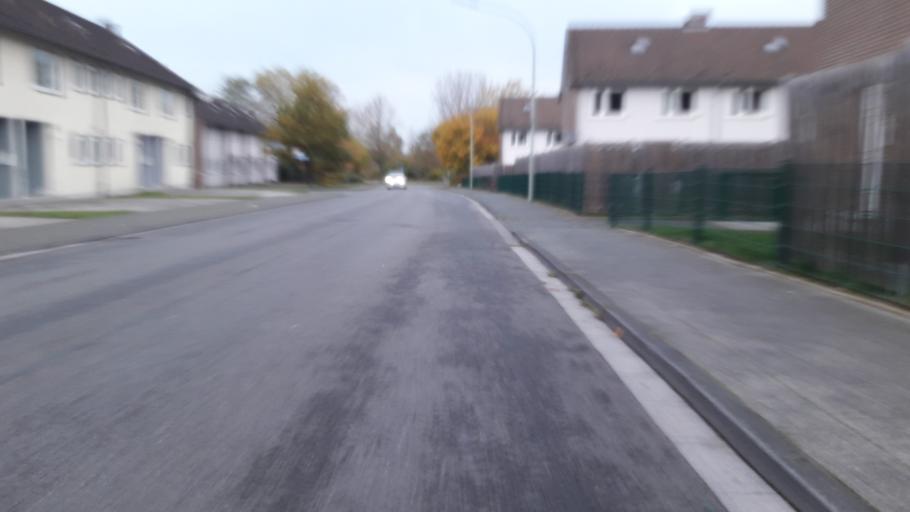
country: DE
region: North Rhine-Westphalia
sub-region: Regierungsbezirk Detmold
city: Paderborn
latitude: 51.7282
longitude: 8.7827
